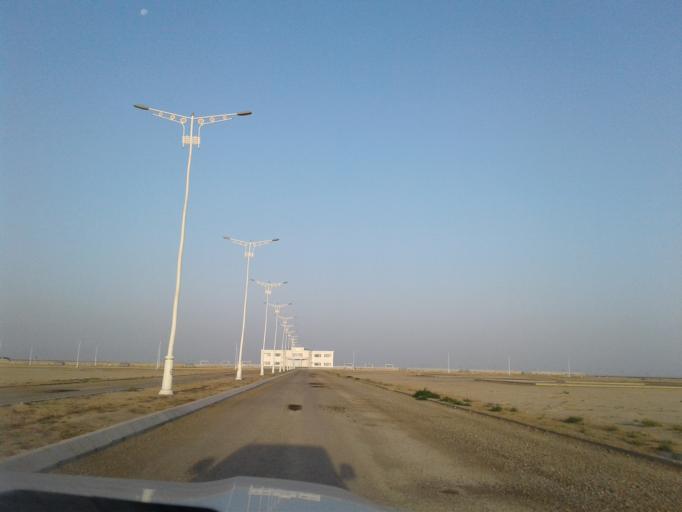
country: IR
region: Golestan
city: Aq Qayeh
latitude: 37.7058
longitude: 54.7467
